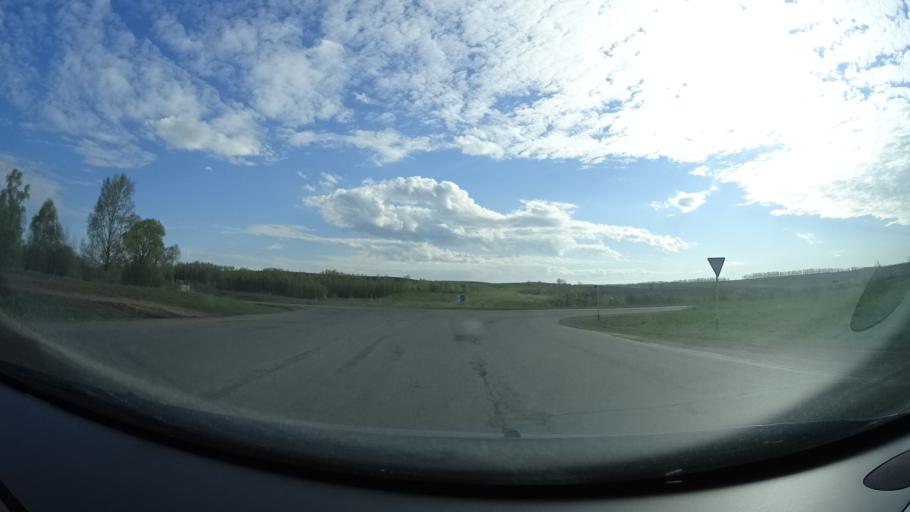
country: RU
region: Bashkortostan
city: Blagoveshchensk
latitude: 55.1108
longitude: 55.8404
